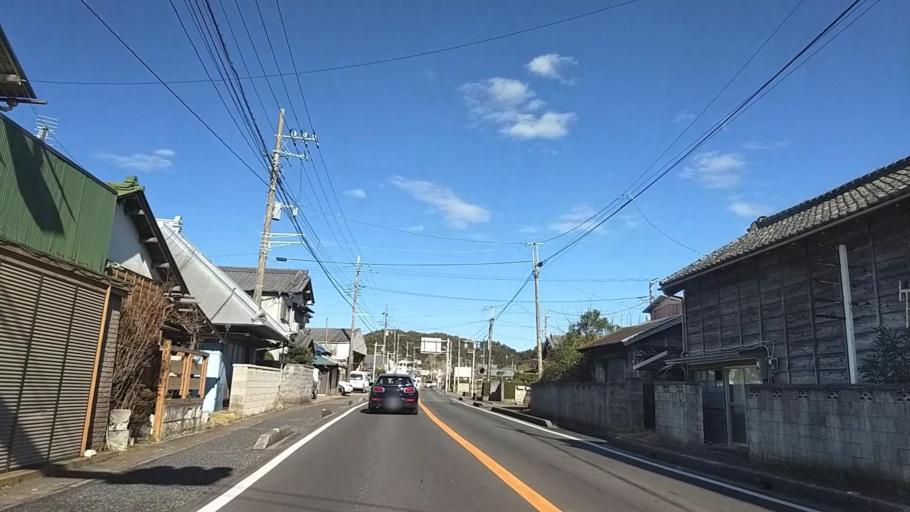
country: JP
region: Chiba
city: Katsuura
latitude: 35.1893
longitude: 140.3583
